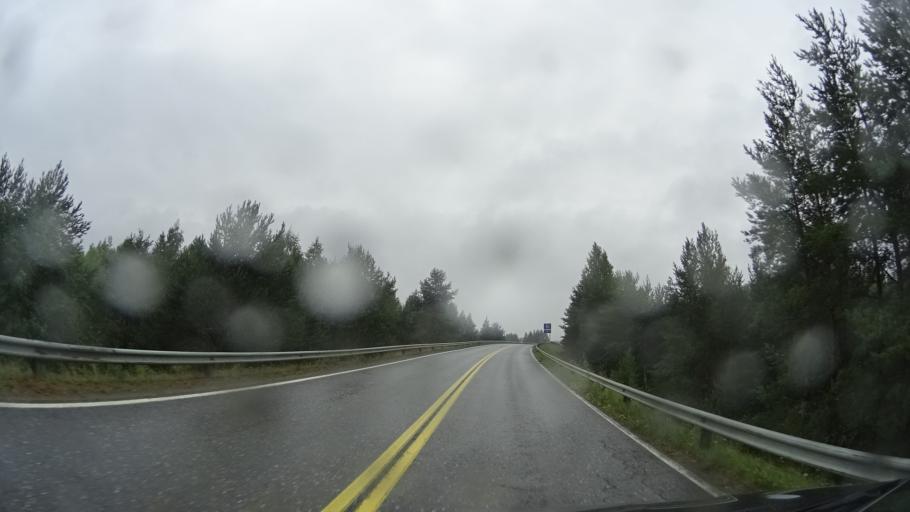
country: FI
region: North Karelia
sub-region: Keski-Karjala
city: Raeaekkylae
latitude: 62.3131
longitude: 29.5158
